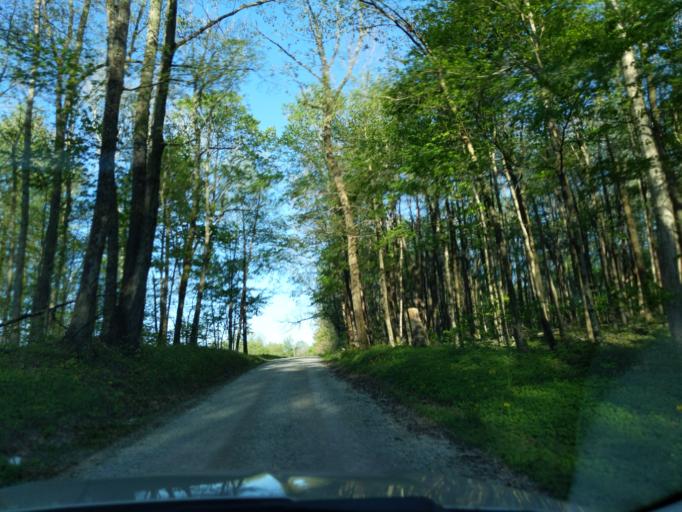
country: US
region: Indiana
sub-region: Decatur County
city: Westport
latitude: 39.2002
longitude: -85.4400
